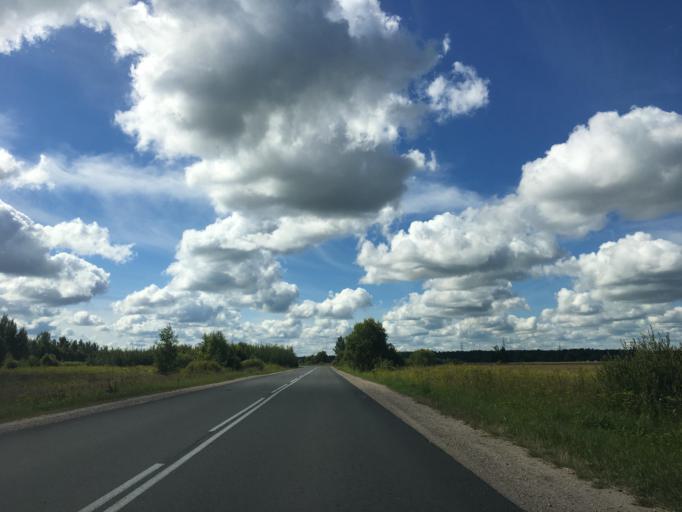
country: RU
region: Pskov
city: Pskov
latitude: 57.7726
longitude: 28.1618
